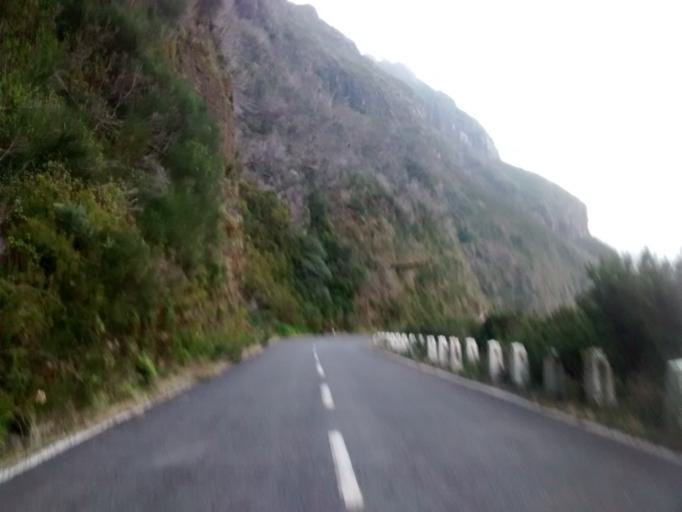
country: PT
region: Madeira
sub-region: Sao Vicente
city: Sao Vicente
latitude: 32.7446
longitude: -17.0436
